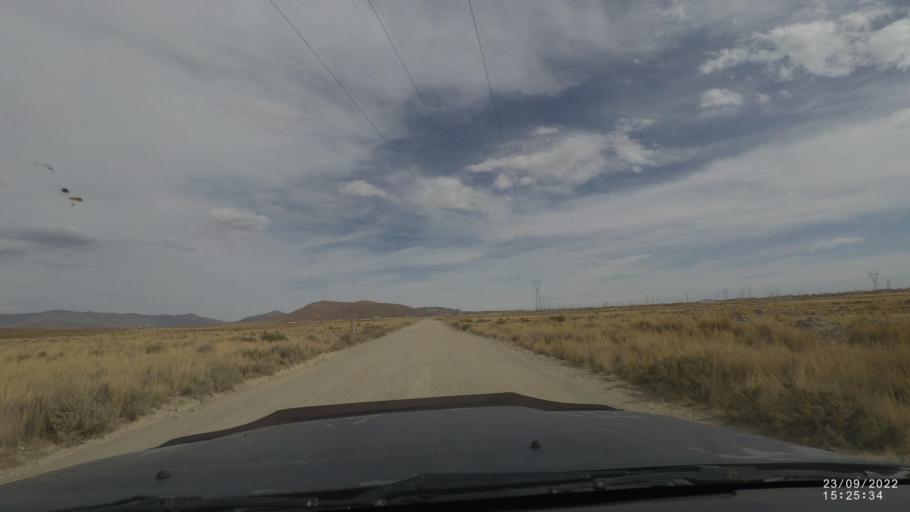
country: BO
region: Oruro
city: Oruro
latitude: -17.9463
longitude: -67.0396
